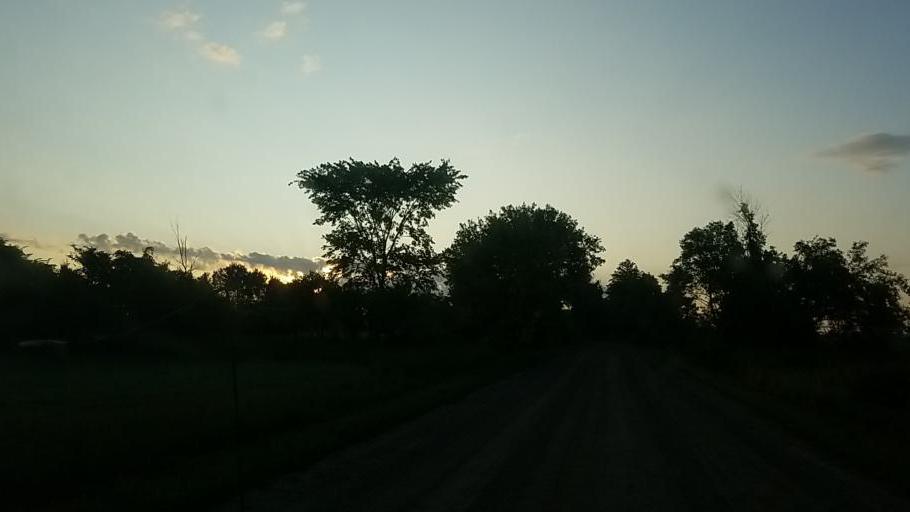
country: US
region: Michigan
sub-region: Osceola County
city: Evart
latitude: 43.9152
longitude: -85.1935
